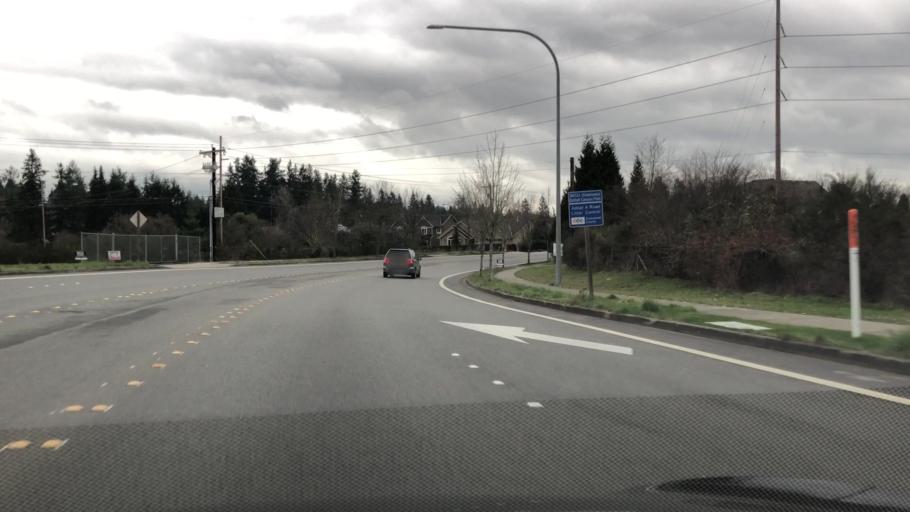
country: US
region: Washington
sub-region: Snohomish County
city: North Creek
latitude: 47.8117
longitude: -122.1814
